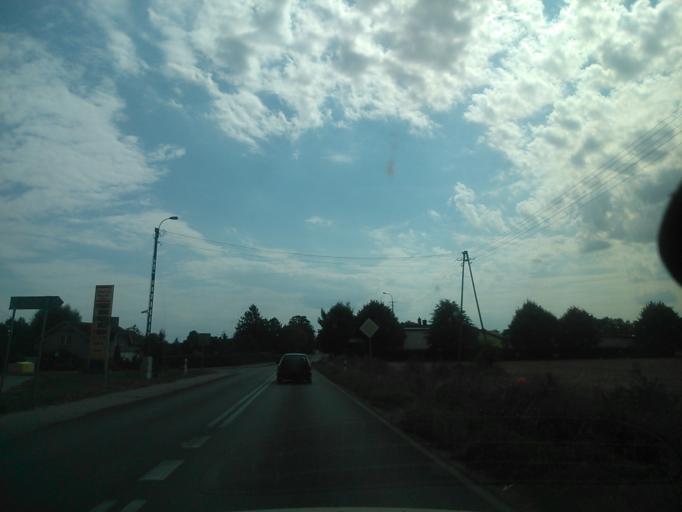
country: PL
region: Warmian-Masurian Voivodeship
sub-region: Powiat dzialdowski
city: Ilowo -Osada
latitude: 53.1770
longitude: 20.2962
